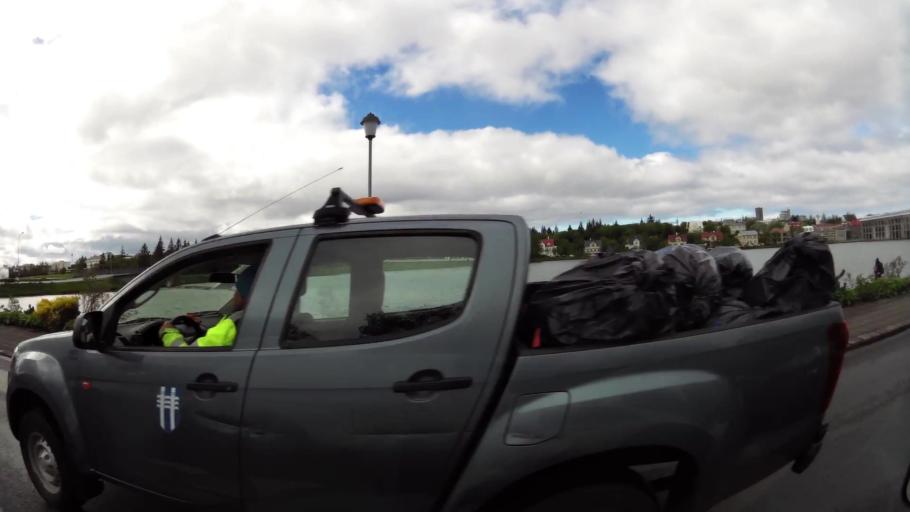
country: IS
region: Capital Region
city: Kopavogur
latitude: 64.1435
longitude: -21.9401
